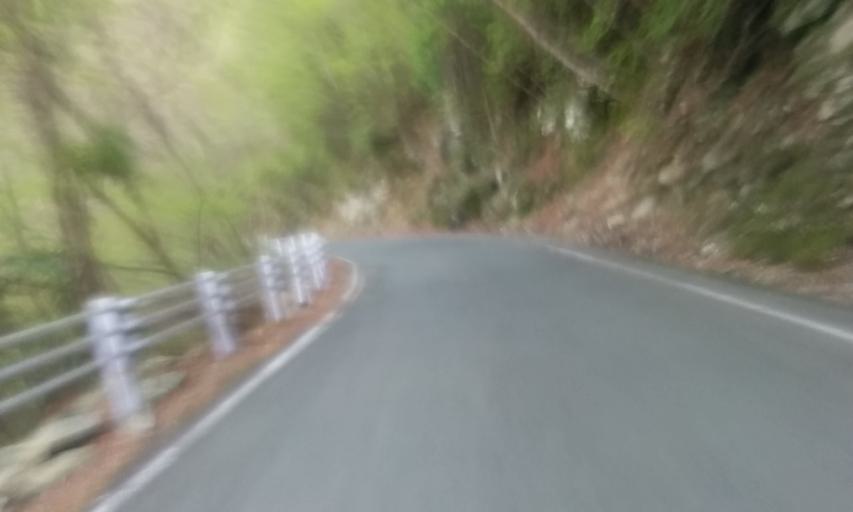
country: JP
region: Ehime
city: Saijo
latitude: 33.7964
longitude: 133.2683
